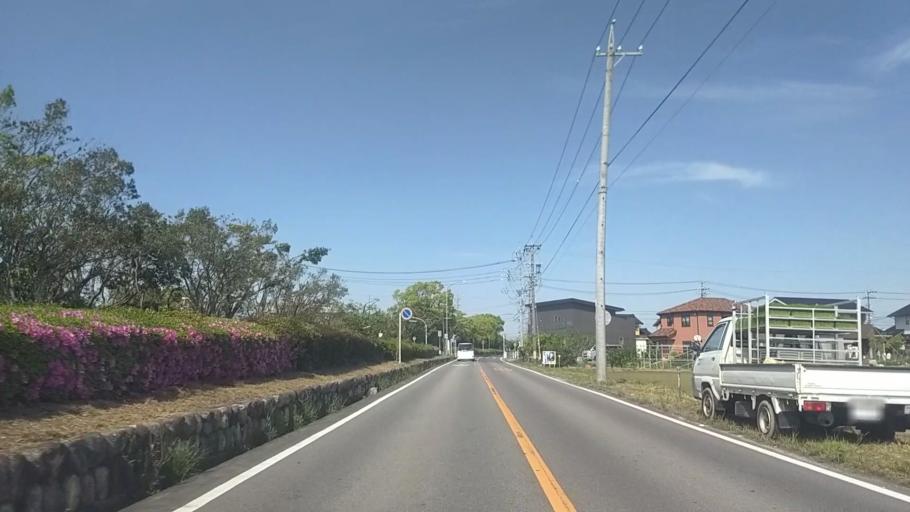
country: JP
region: Aichi
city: Anjo
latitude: 34.9738
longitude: 137.0766
